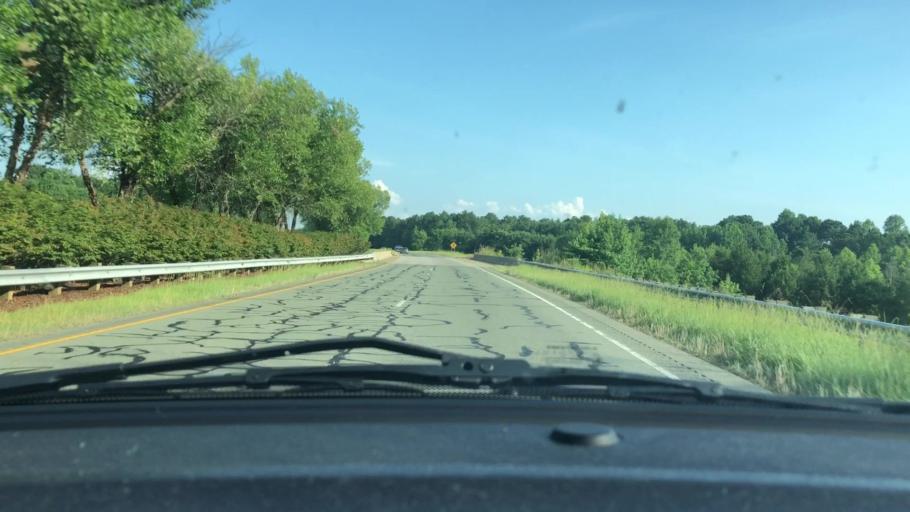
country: US
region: North Carolina
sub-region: Chatham County
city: Siler City
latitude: 35.6950
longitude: -79.4283
